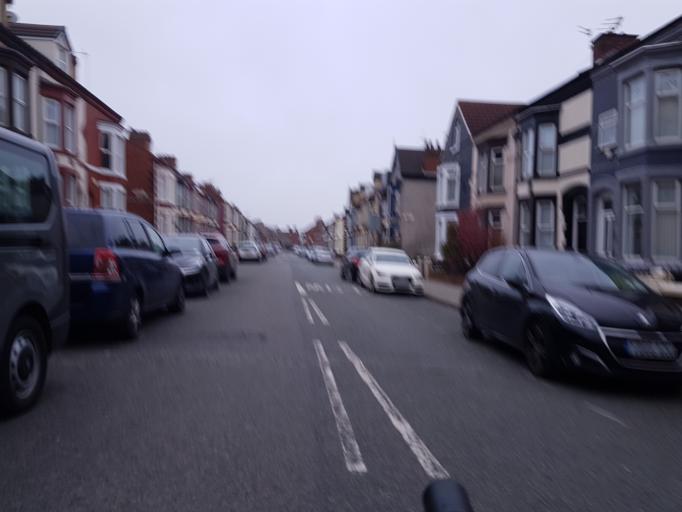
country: GB
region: England
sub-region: Liverpool
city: Liverpool
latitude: 53.4454
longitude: -2.9722
